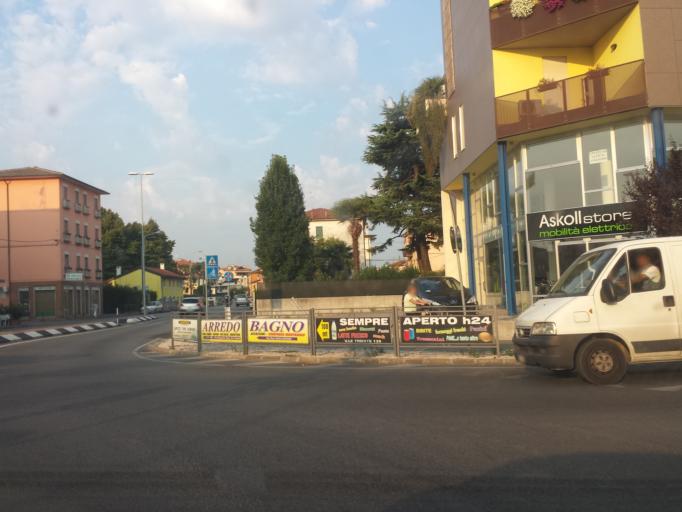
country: IT
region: Veneto
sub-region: Provincia di Vicenza
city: Vicenza
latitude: 45.5596
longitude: 11.5613
